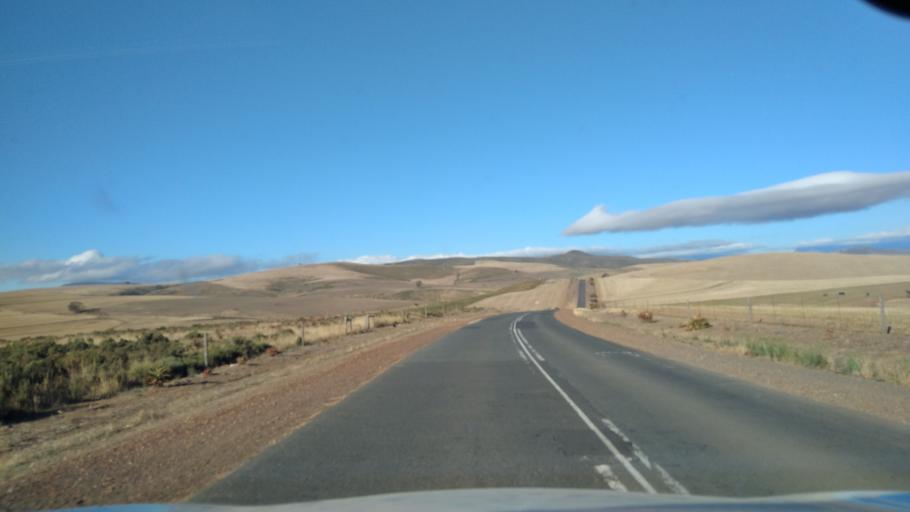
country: ZA
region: Western Cape
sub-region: Overberg District Municipality
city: Caledon
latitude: -34.1740
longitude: 19.2821
